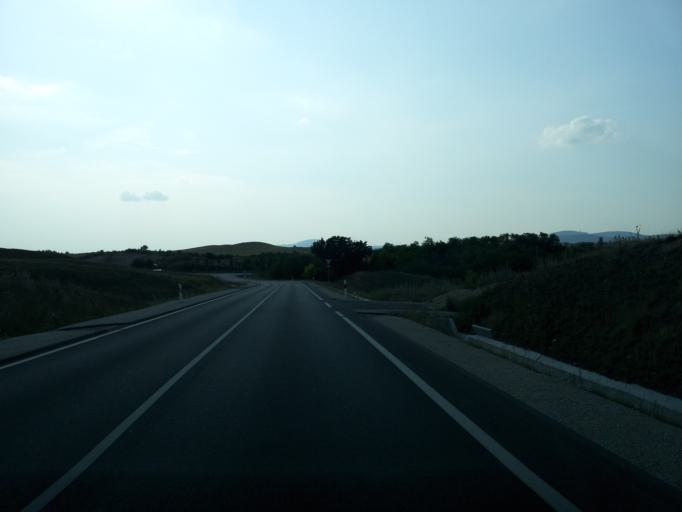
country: HU
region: Veszprem
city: Hajmasker
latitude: 47.1375
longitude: 18.0245
